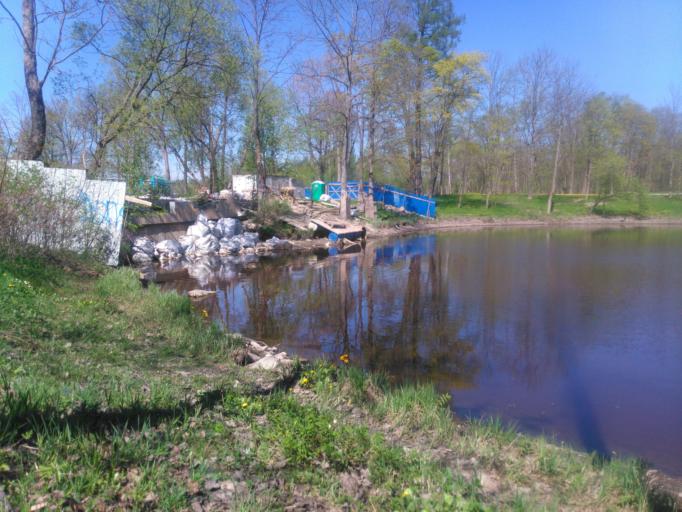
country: RU
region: St.-Petersburg
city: Pushkin
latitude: 59.7235
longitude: 30.3715
